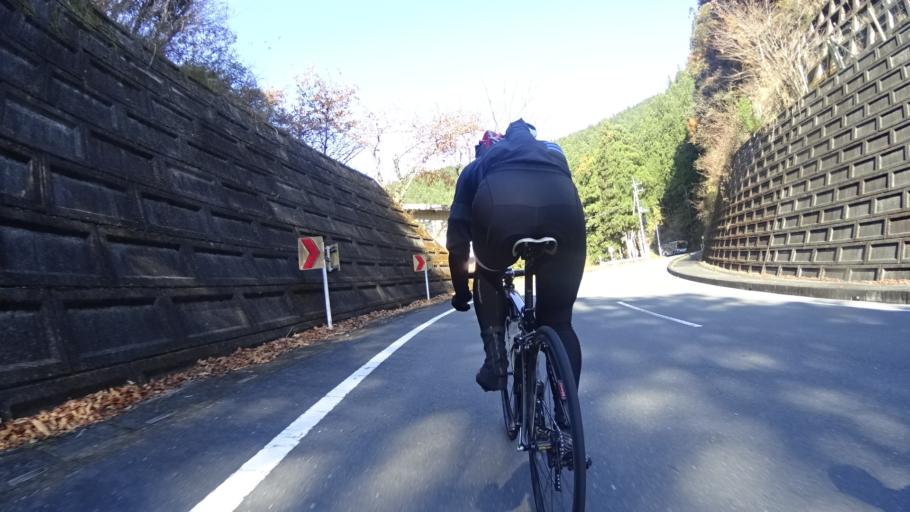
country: JP
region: Saitama
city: Chichibu
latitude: 35.9050
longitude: 139.1579
